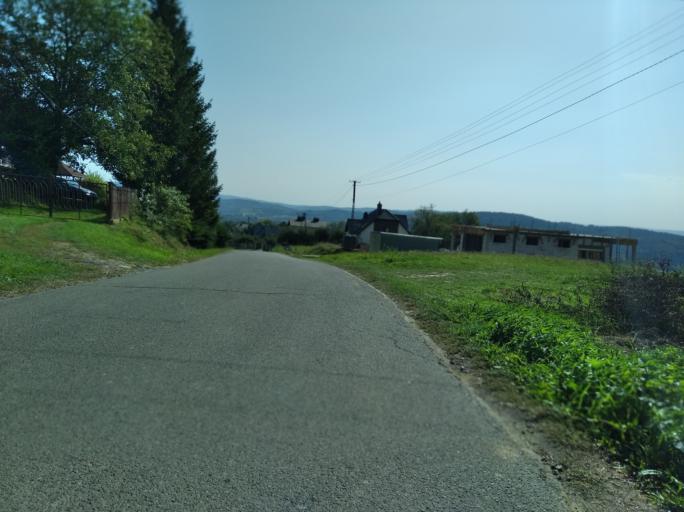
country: PL
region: Subcarpathian Voivodeship
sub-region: Powiat strzyzowski
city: Czudec
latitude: 49.9539
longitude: 21.8300
